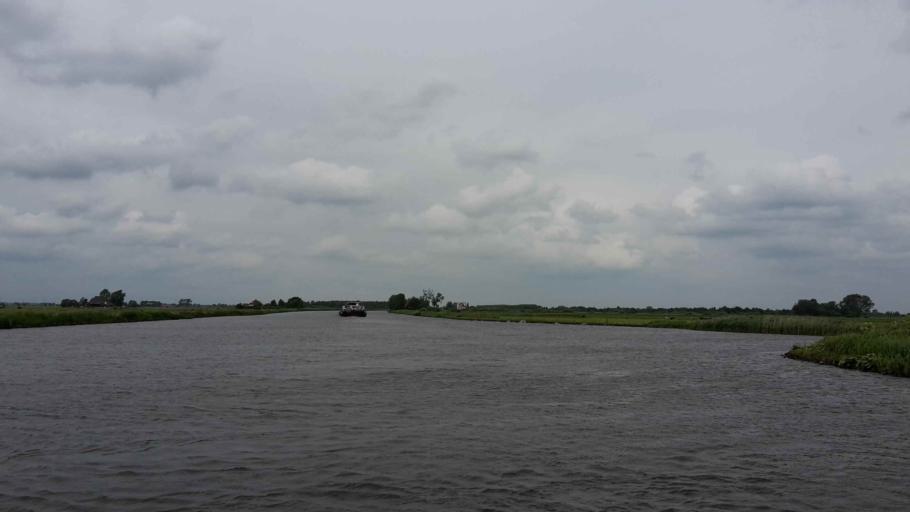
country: NL
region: Friesland
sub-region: Gemeente Boarnsterhim
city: Warten
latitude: 53.1166
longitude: 5.8771
